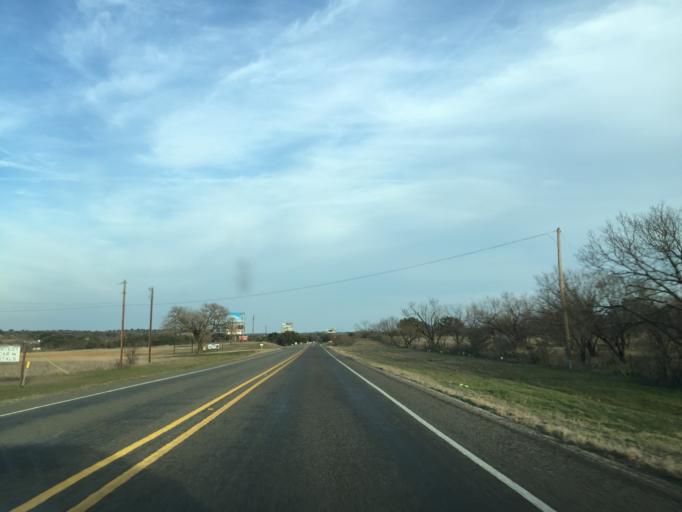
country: US
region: Texas
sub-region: Llano County
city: Llano
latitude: 30.7617
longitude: -98.6366
